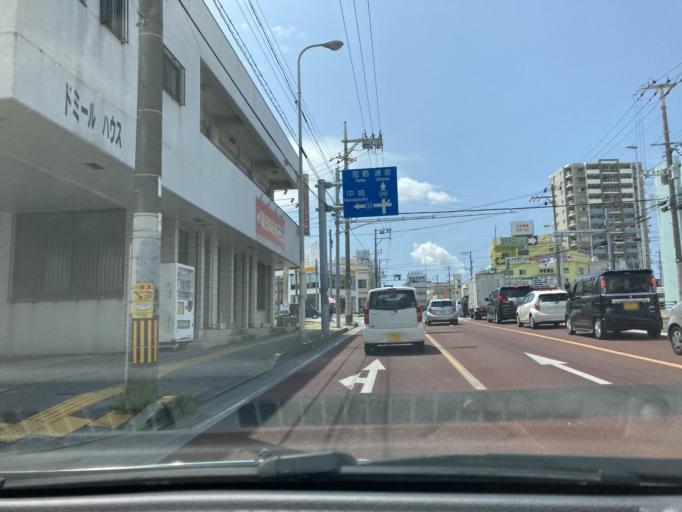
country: JP
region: Okinawa
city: Ginowan
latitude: 26.2630
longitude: 127.7620
